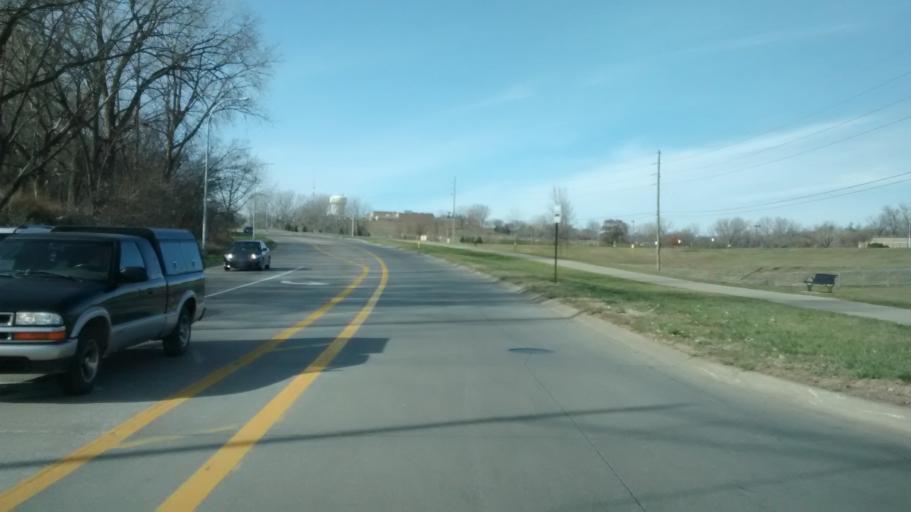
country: US
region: Iowa
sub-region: Woodbury County
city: Sioux City
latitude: 42.5408
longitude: -96.3810
